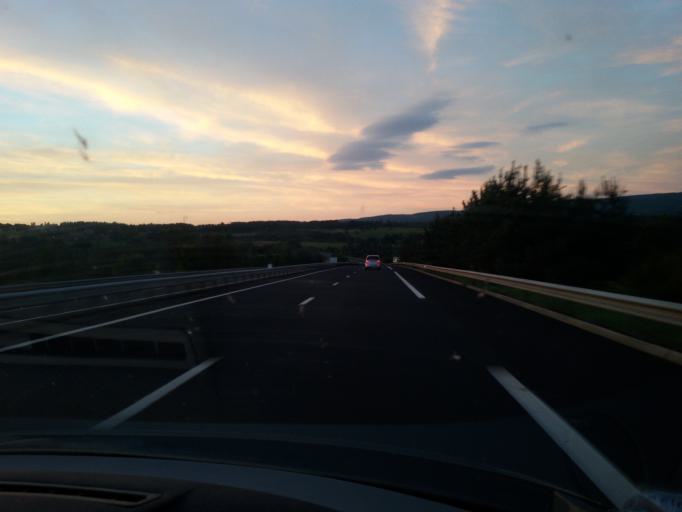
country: FR
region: Auvergne
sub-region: Departement du Cantal
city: Saint-Flour
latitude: 44.9853
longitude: 3.1856
